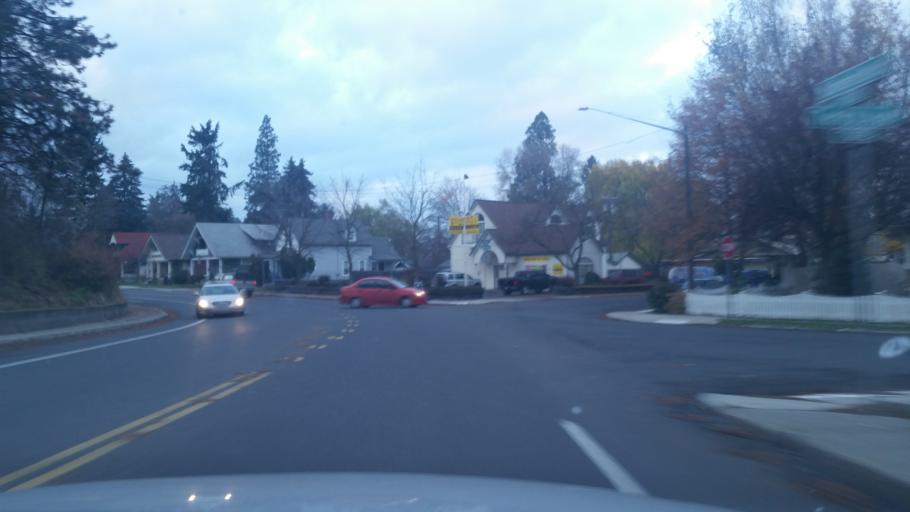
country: US
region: Washington
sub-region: Spokane County
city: Spokane
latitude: 47.6457
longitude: -117.4002
